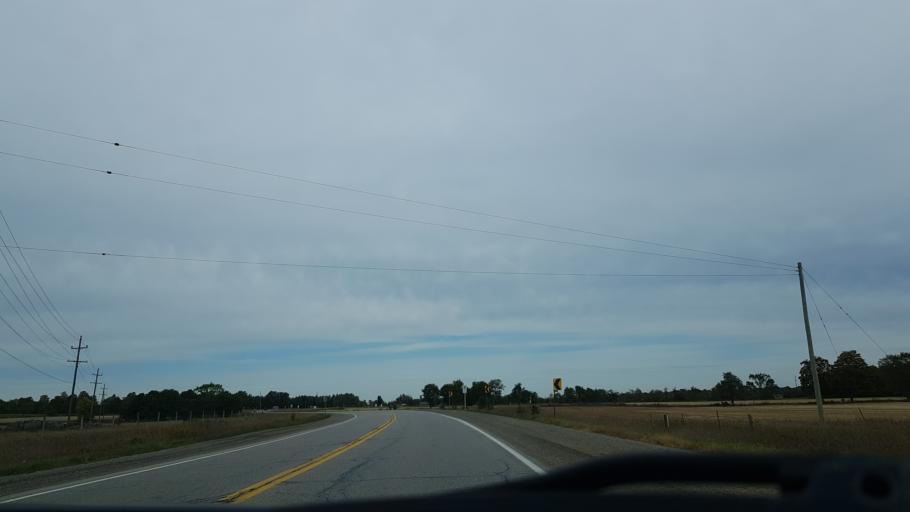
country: CA
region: Ontario
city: Orangeville
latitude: 43.8236
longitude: -80.0364
